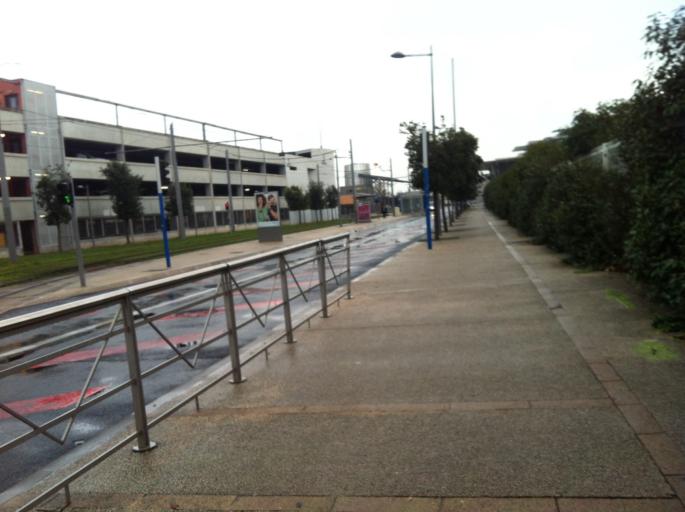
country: FR
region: Languedoc-Roussillon
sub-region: Departement de l'Herault
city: Montferrier-sur-Lez
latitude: 43.6357
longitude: 3.8474
